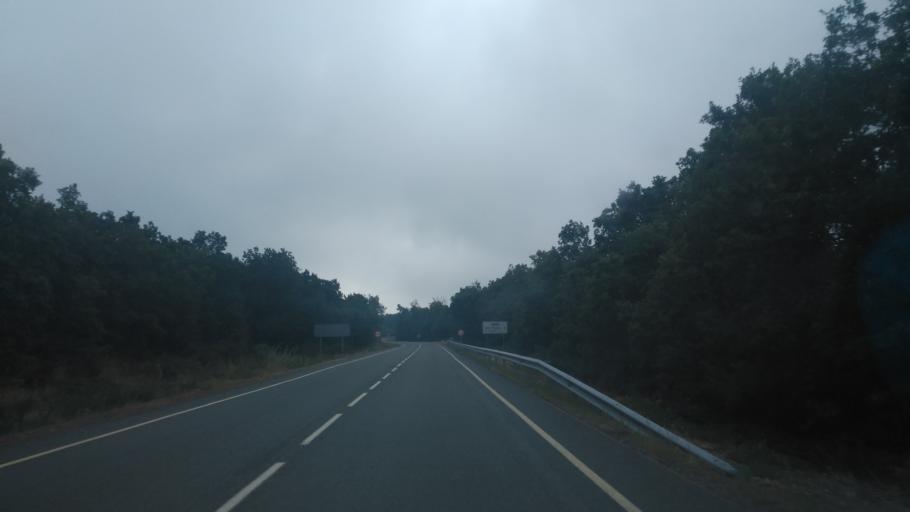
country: ES
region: Castille and Leon
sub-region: Provincia de Salamanca
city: Cilleros de la Bastida
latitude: 40.5614
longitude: -6.0692
